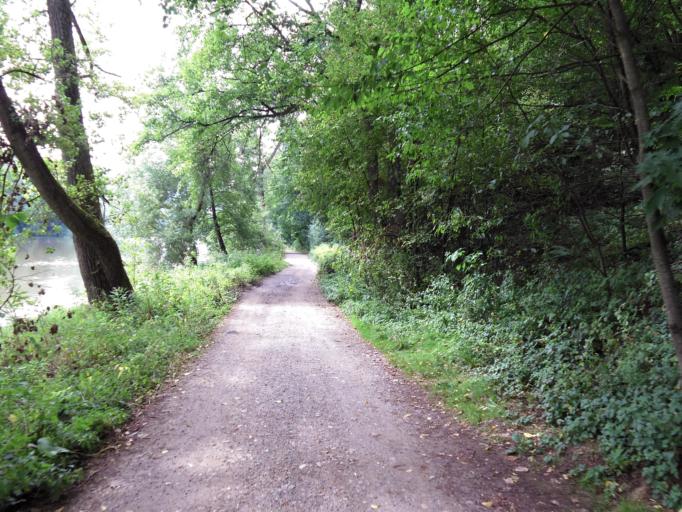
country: CZ
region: Central Bohemia
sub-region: Okres Benesov
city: Cercany
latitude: 49.8780
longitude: 14.7274
